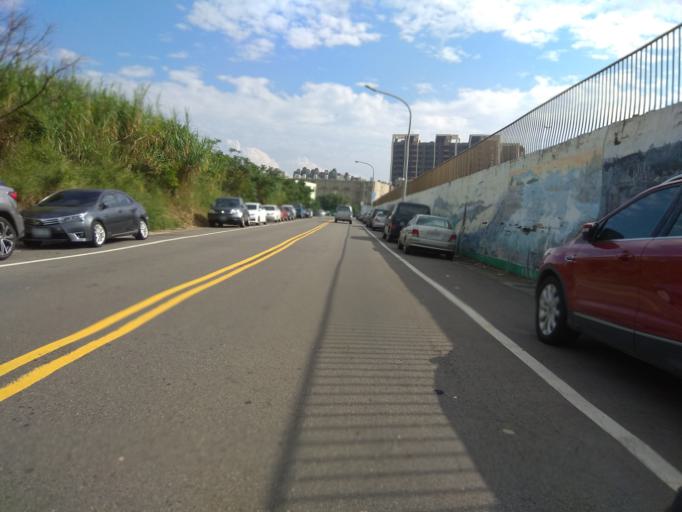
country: TW
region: Taiwan
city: Taoyuan City
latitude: 25.0646
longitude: 121.1921
